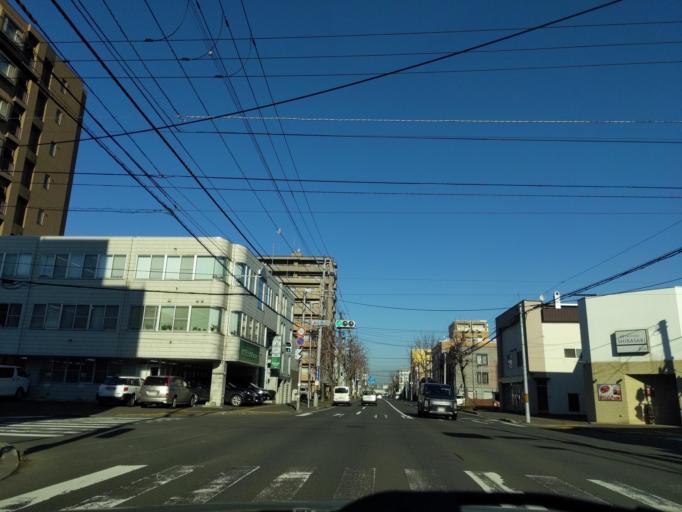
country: JP
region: Hokkaido
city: Sapporo
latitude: 43.0678
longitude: 141.3244
